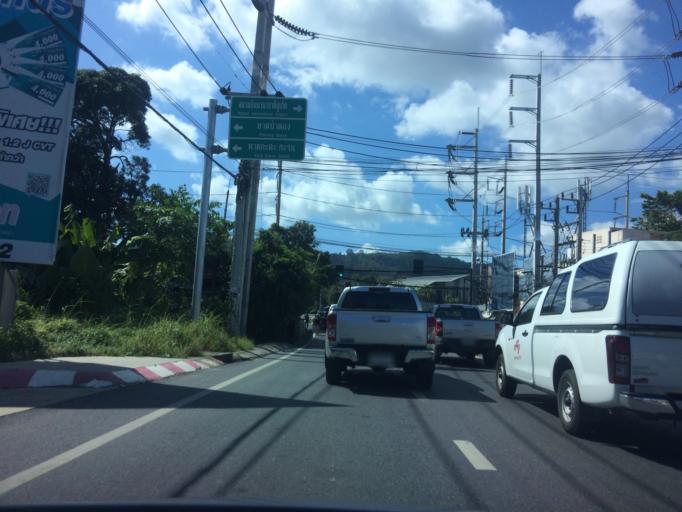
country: TH
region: Phuket
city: Mueang Phuket
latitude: 7.8743
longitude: 98.3638
